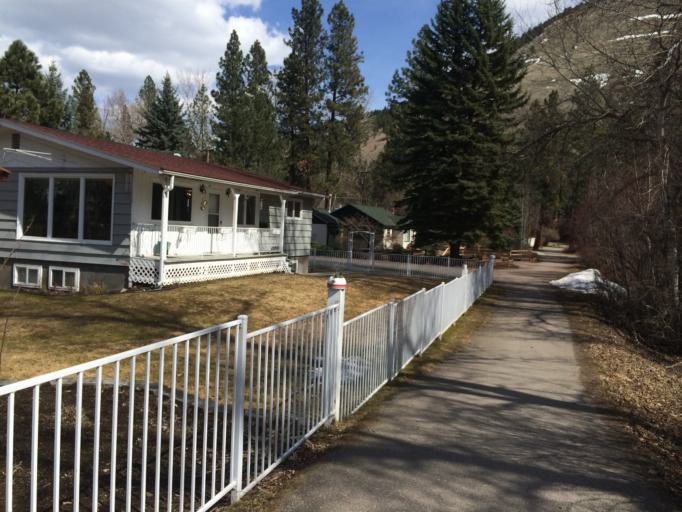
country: US
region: Montana
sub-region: Missoula County
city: Missoula
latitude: 46.8794
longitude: -113.9745
